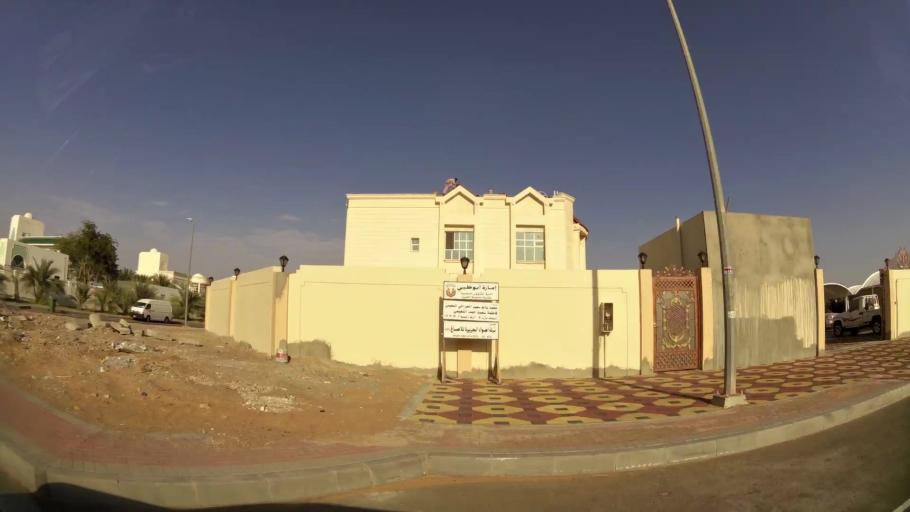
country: AE
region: Abu Dhabi
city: Al Ain
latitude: 24.0570
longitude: 55.8415
